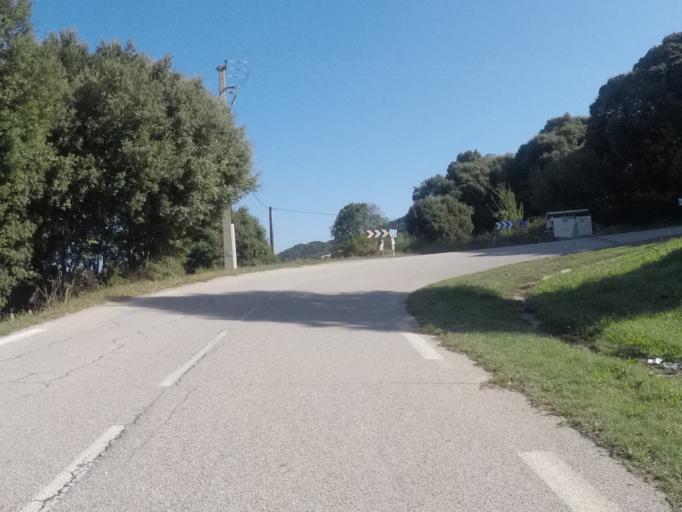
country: FR
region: Corsica
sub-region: Departement de la Corse-du-Sud
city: Olmeto
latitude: 41.7475
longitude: 8.9291
